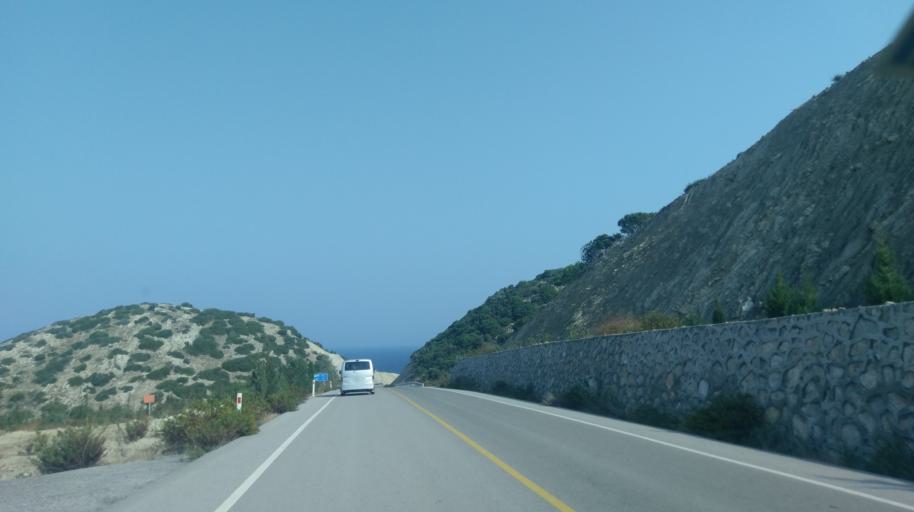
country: CY
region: Ammochostos
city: Leonarisso
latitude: 35.4614
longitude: 34.0196
